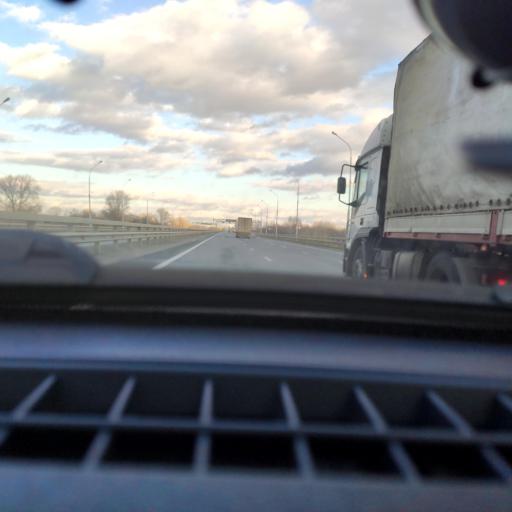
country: RU
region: Bashkortostan
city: Ufa
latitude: 54.6443
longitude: 55.9832
